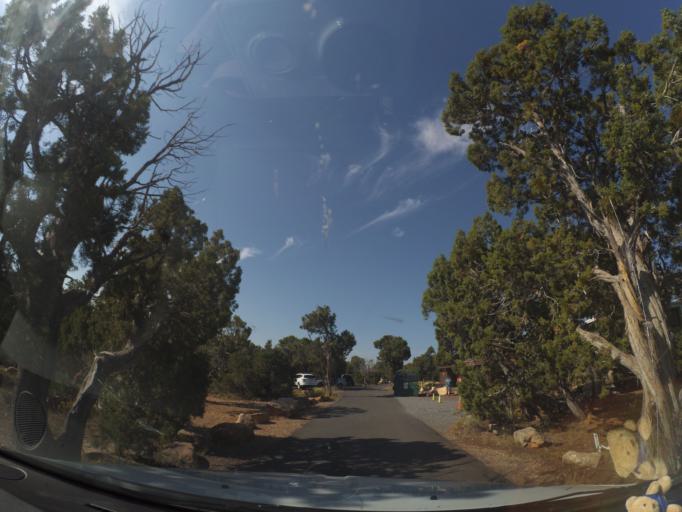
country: US
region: Arizona
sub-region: Coconino County
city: Grand Canyon
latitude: 36.0391
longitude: -111.8227
